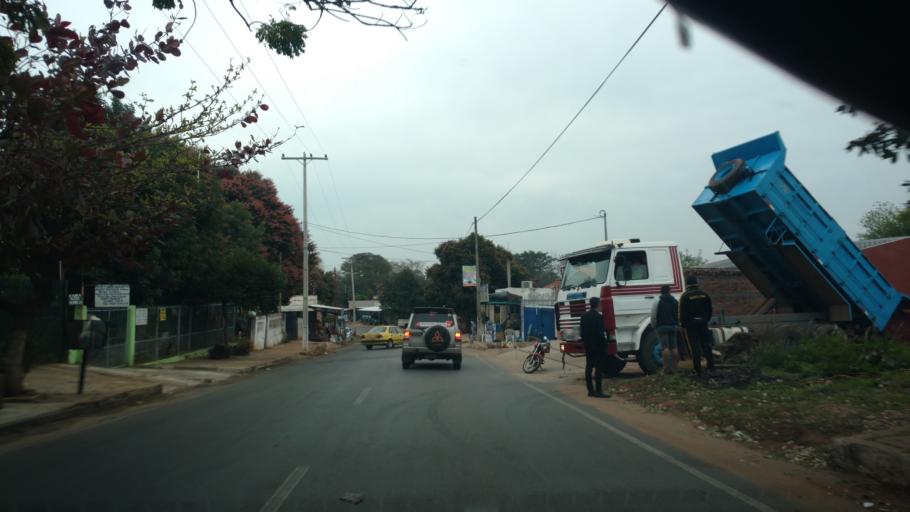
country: PY
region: Central
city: Capiata
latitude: -25.3592
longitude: -57.4731
